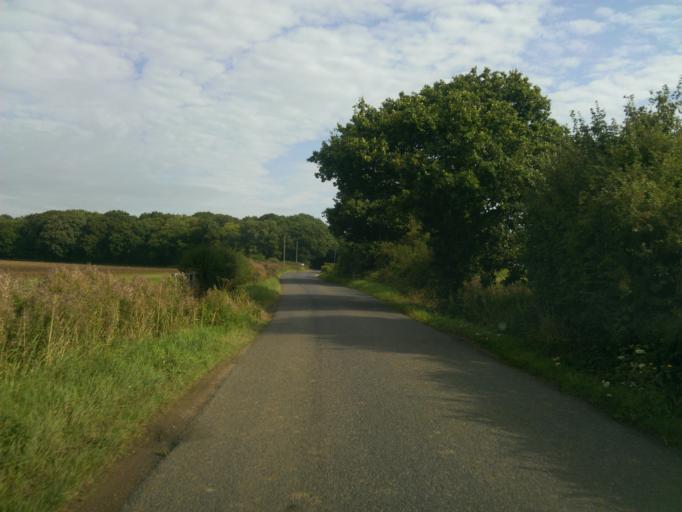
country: GB
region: England
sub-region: Essex
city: Saint Osyth
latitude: 51.8306
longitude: 1.1031
